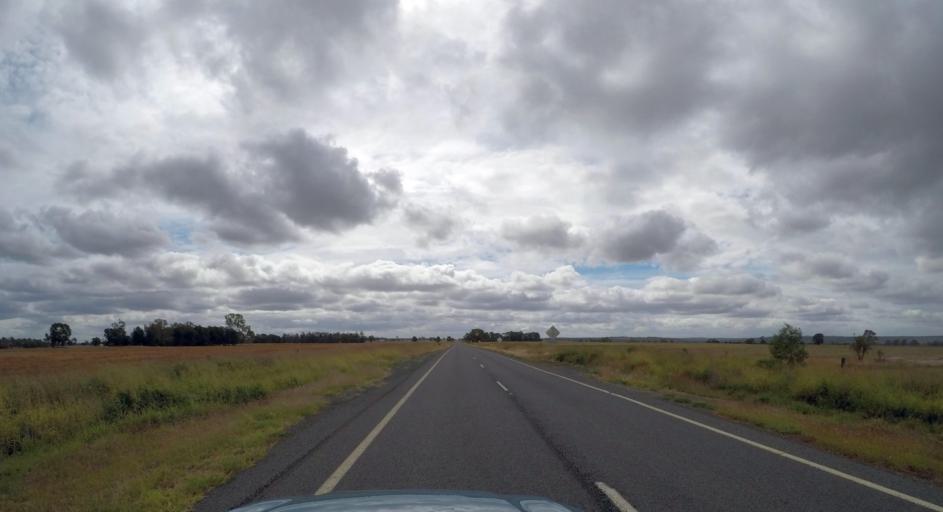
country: AU
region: Queensland
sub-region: South Burnett
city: Kingaroy
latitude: -26.3902
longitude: 151.2444
